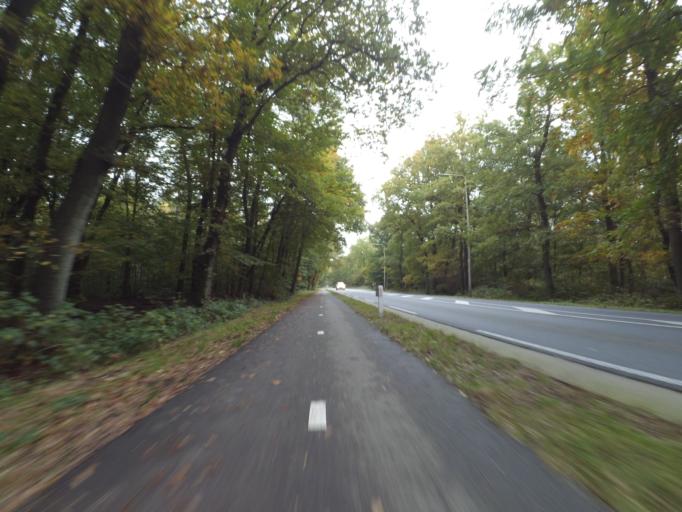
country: NL
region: Gelderland
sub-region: Gemeente Ermelo
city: Ermelo
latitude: 52.3044
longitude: 5.6675
